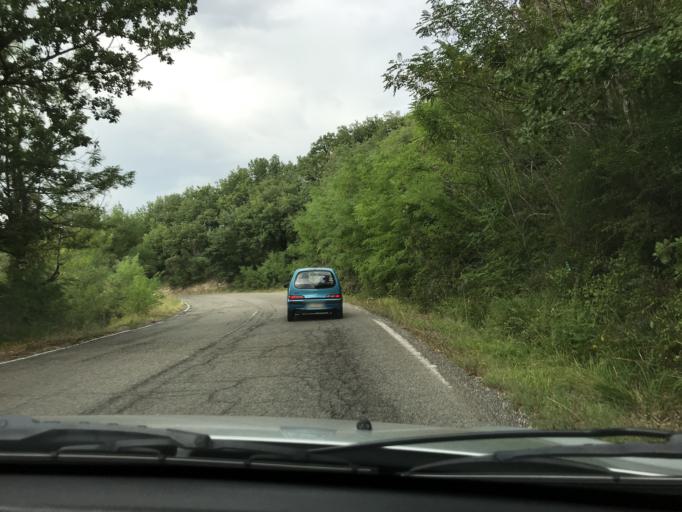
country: IT
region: Umbria
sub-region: Provincia di Terni
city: Montecchio
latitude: 42.6424
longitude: 12.2837
